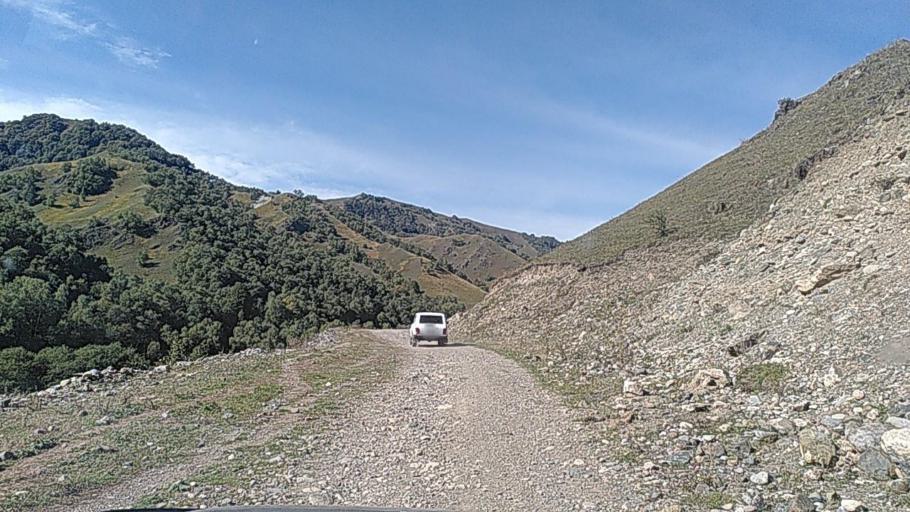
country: RU
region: Kabardino-Balkariya
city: Kamennomostskoye
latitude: 43.7188
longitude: 42.8854
